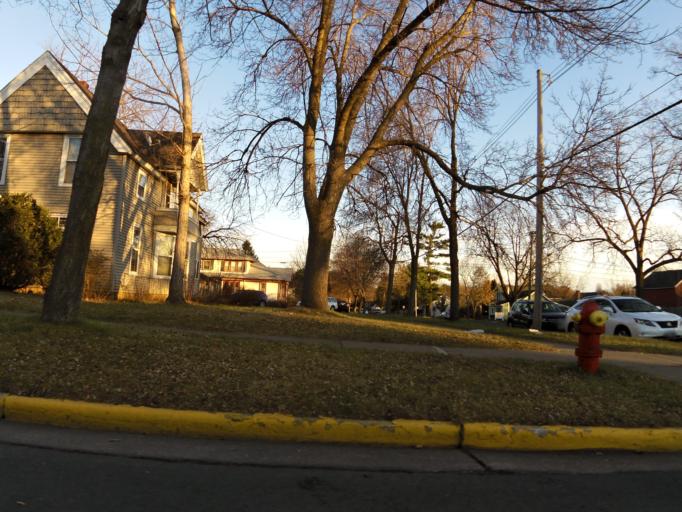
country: US
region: Wisconsin
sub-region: Pierce County
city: River Falls
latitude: 44.8576
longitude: -92.6216
